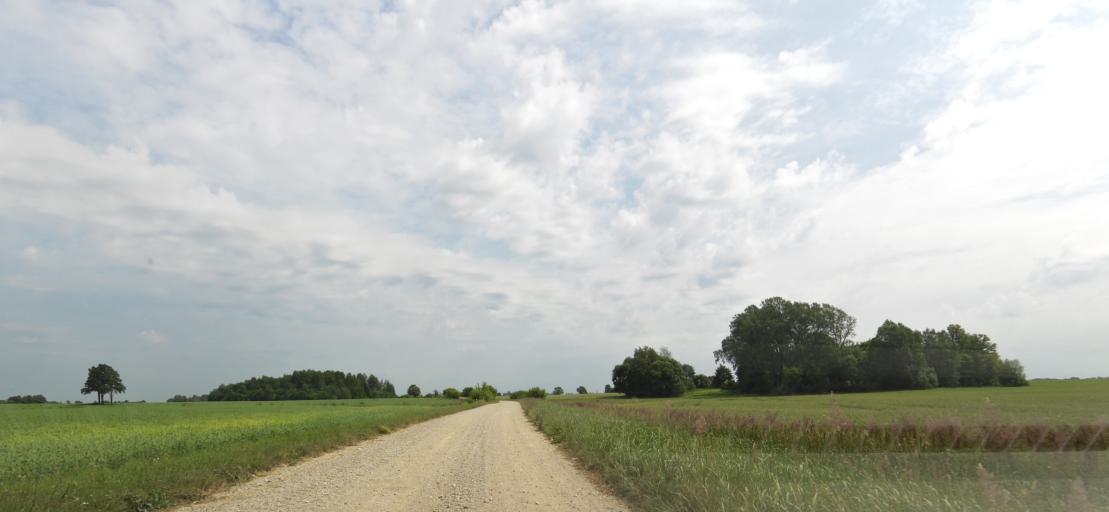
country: LT
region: Panevezys
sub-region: Birzai
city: Birzai
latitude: 56.3205
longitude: 24.6907
